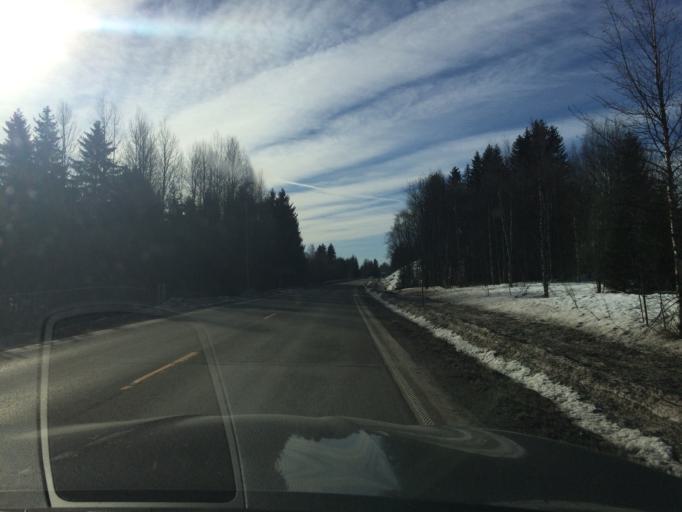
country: NO
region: Hedmark
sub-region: Trysil
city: Innbygda
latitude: 61.3133
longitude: 12.2557
